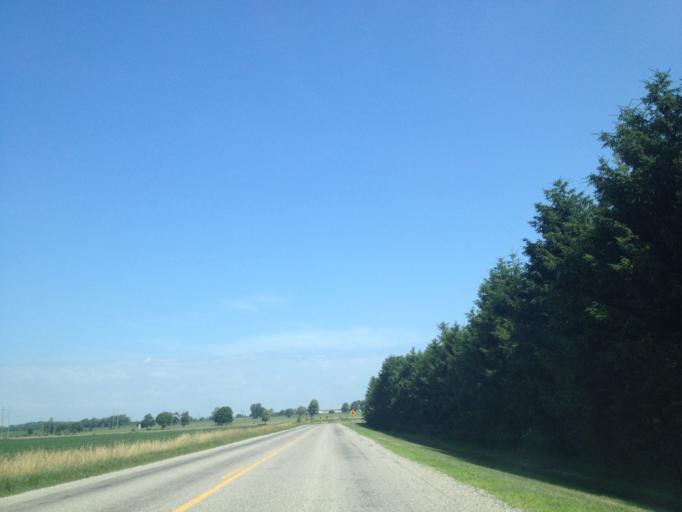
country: CA
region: Ontario
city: London
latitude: 43.1945
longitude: -81.2407
